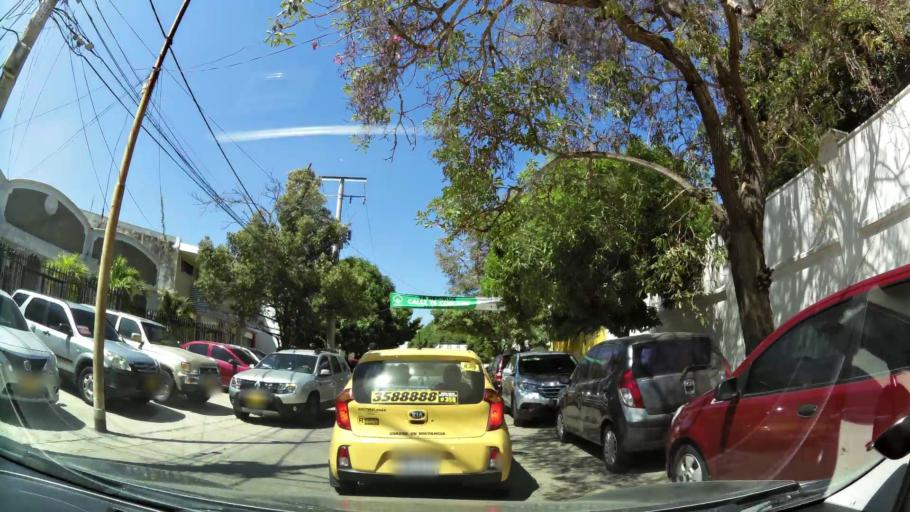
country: CO
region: Atlantico
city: Barranquilla
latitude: 10.9991
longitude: -74.8079
